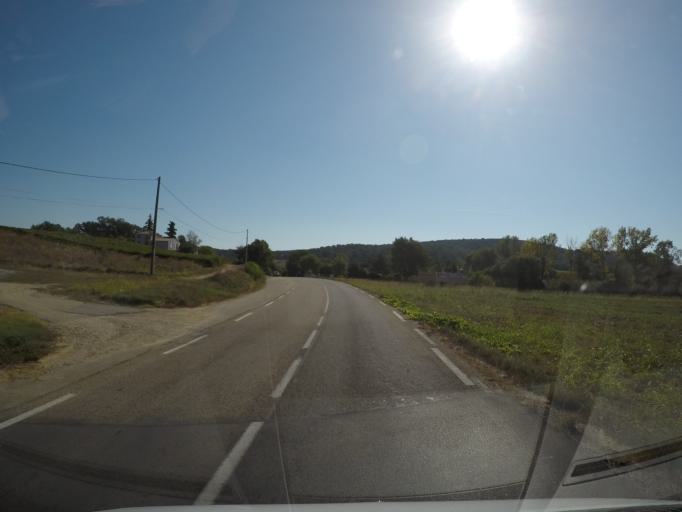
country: FR
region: Languedoc-Roussillon
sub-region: Departement du Gard
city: Ledignan
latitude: 44.0069
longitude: 4.1237
